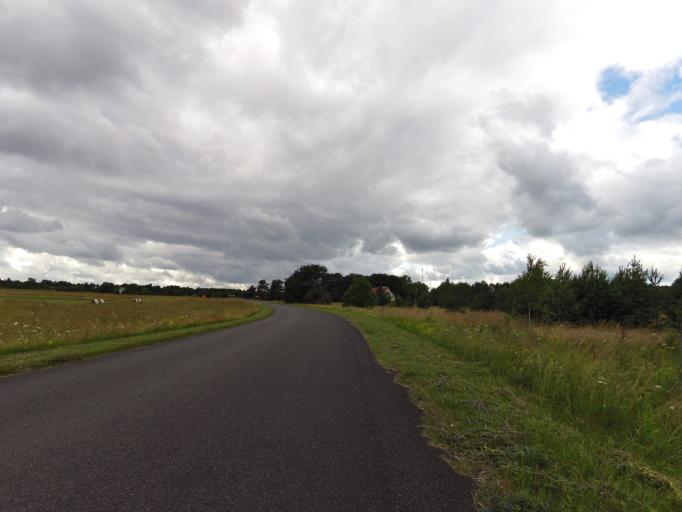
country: EE
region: Laeaene
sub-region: Vormsi vald
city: Hullo
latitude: 58.9884
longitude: 23.2528
